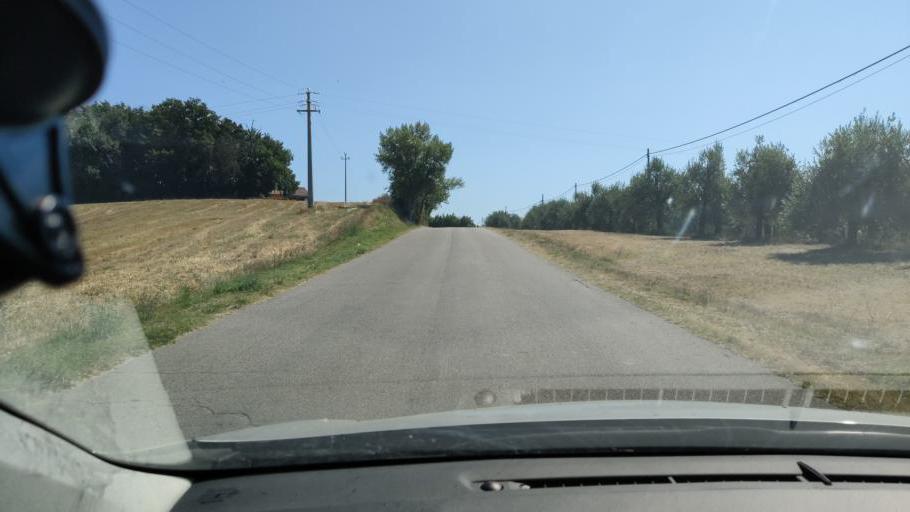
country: IT
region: Umbria
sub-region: Provincia di Terni
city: Fornole
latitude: 42.5263
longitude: 12.4396
